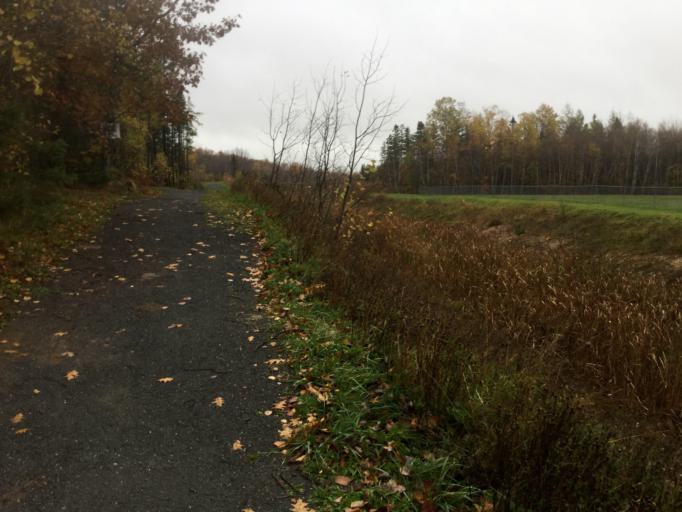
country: CA
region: Nova Scotia
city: New Glasgow
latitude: 45.5490
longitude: -62.6778
